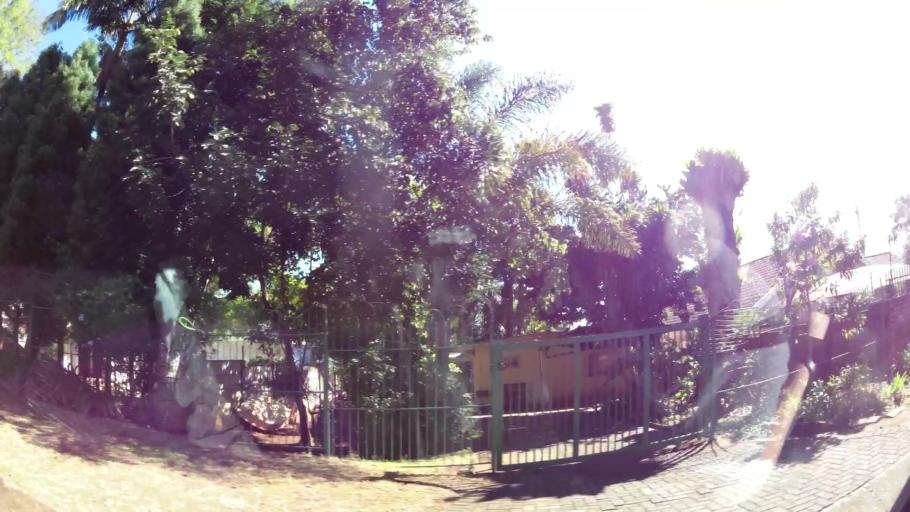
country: ZA
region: Limpopo
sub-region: Mopani District Municipality
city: Tzaneen
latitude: -23.8344
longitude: 30.1603
